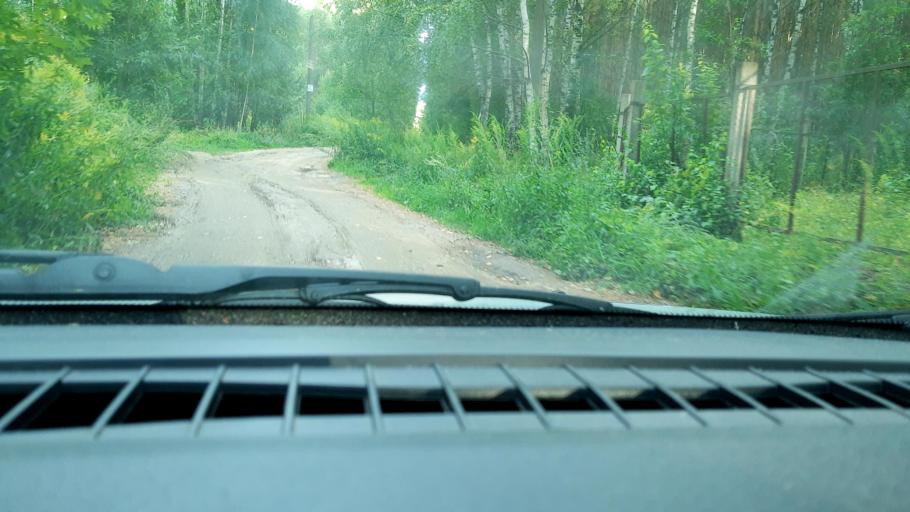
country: RU
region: Nizjnij Novgorod
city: Sitniki
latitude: 56.4518
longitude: 44.0190
